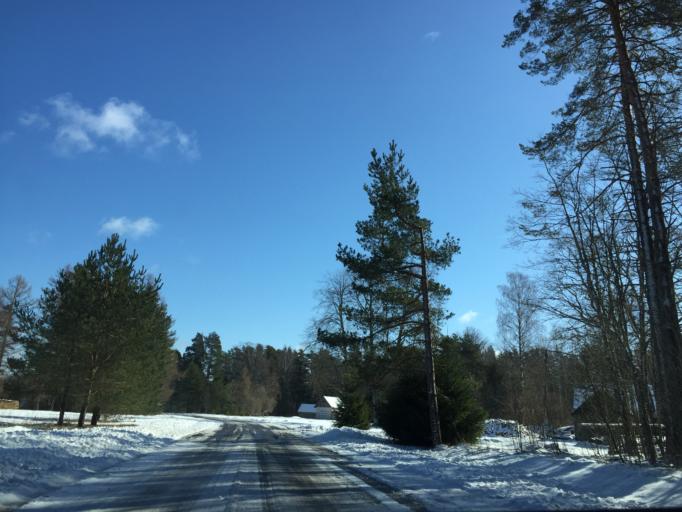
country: LV
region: Aloja
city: Staicele
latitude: 58.0227
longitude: 24.5996
